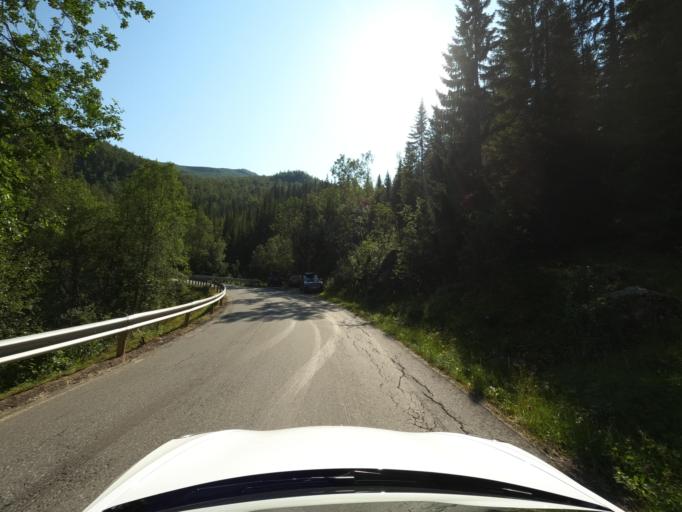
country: NO
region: Nordland
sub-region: Narvik
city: Narvik
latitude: 68.3829
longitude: 17.3463
